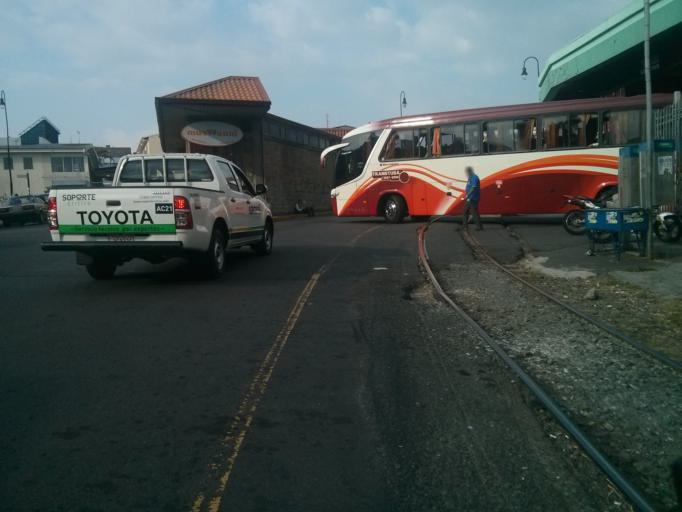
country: CR
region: San Jose
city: San Jose
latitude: 9.9307
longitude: -84.0732
